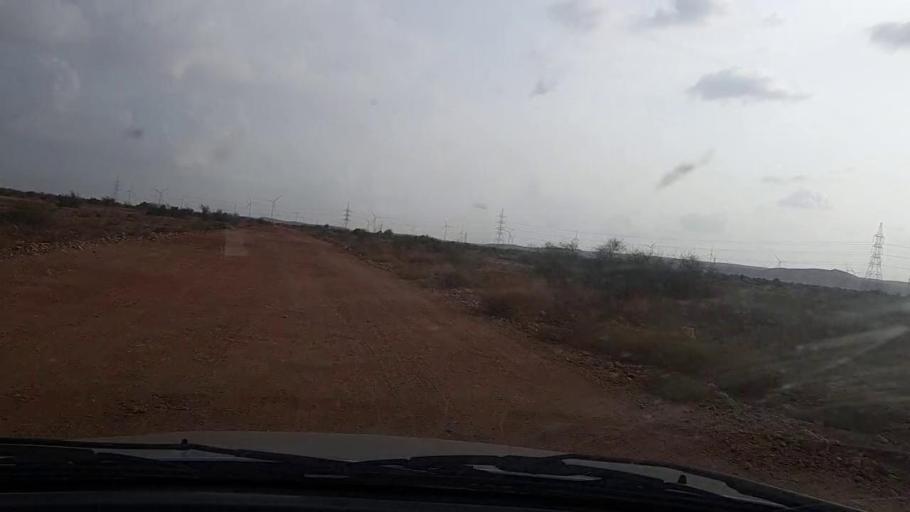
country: PK
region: Sindh
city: Thatta
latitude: 25.0658
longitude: 67.8878
